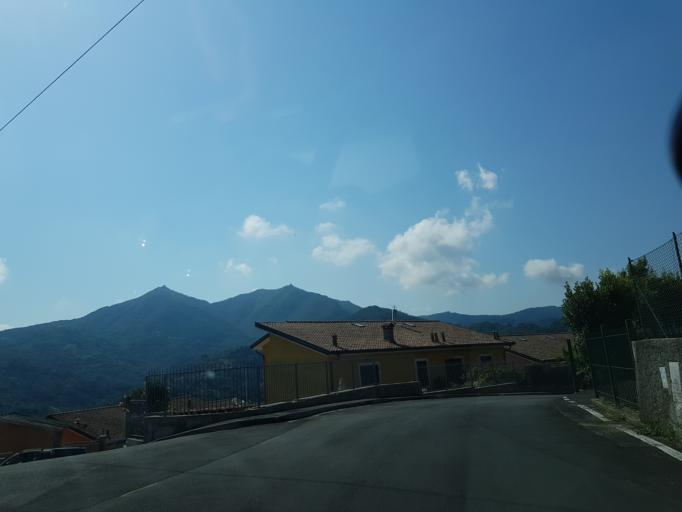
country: IT
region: Liguria
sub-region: Provincia di Genova
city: Manesseno
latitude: 44.4783
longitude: 8.9081
